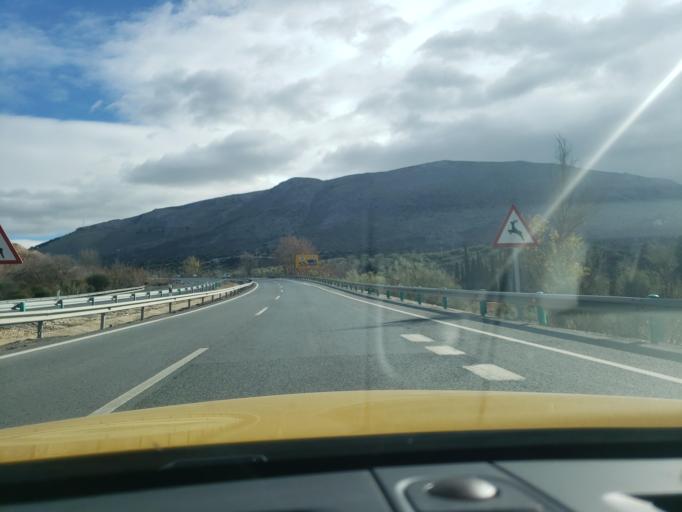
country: ES
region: Andalusia
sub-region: Provincia de Granada
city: Loja
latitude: 37.1576
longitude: -4.2080
